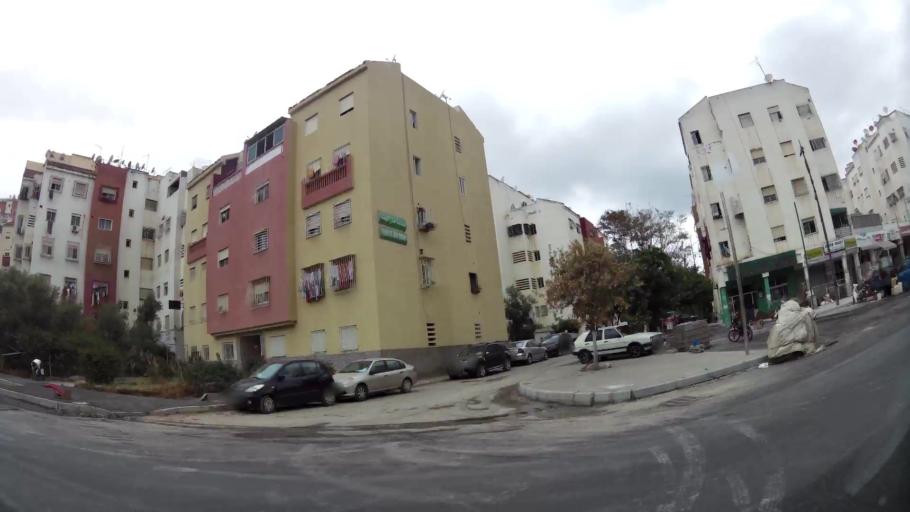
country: MA
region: Rabat-Sale-Zemmour-Zaer
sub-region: Rabat
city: Rabat
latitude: 33.9858
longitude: -6.8045
